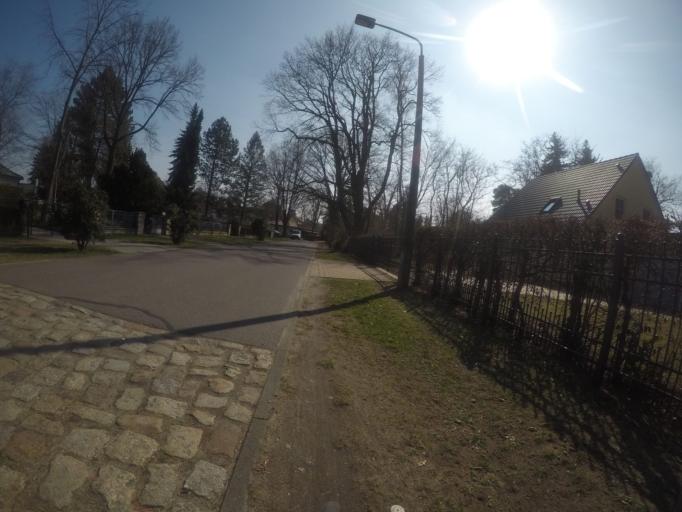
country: DE
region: Brandenburg
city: Konigs Wusterhausen
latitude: 52.2933
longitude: 13.6801
